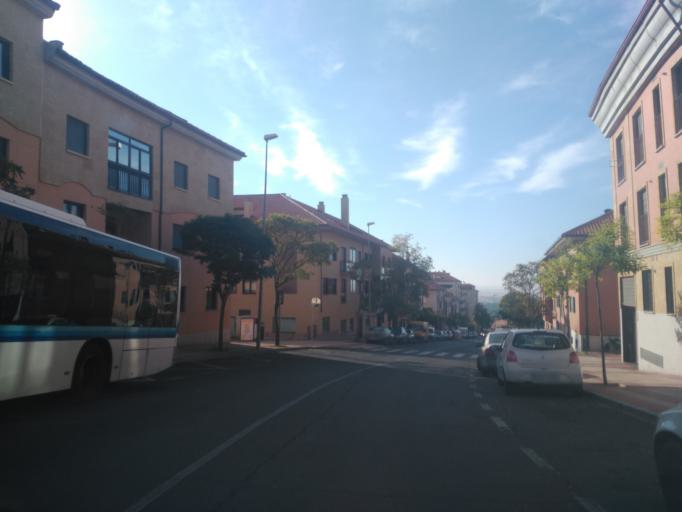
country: ES
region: Castille and Leon
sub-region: Provincia de Salamanca
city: Salamanca
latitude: 40.9753
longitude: -5.6815
